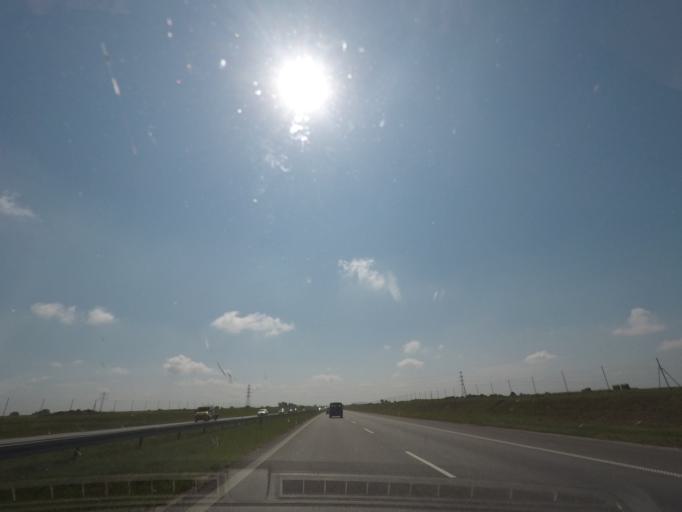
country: PL
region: Kujawsko-Pomorskie
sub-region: Powiat wloclawski
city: Czerniewice
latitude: 52.5546
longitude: 19.0363
